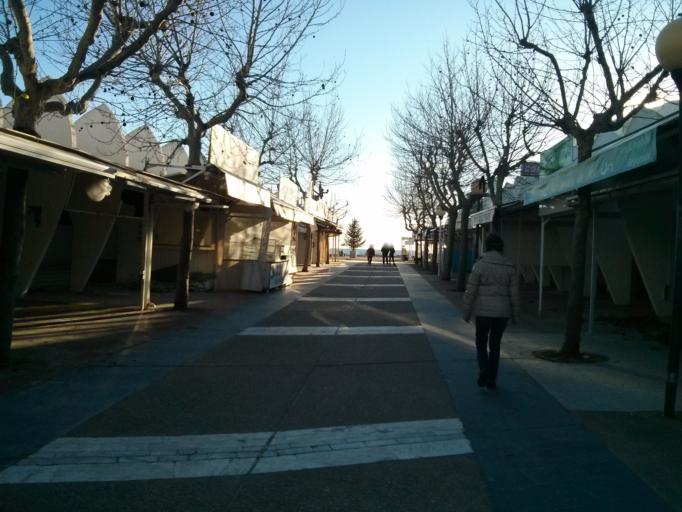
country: FR
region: Languedoc-Roussillon
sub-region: Departement de l'Herault
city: La Grande-Motte
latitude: 43.5588
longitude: 4.0701
